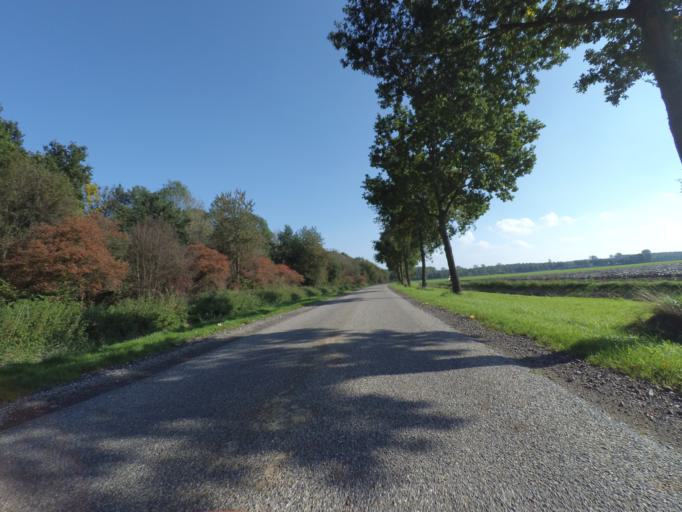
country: NL
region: Flevoland
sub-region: Gemeente Zeewolde
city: Zeewolde
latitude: 52.2925
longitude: 5.5118
